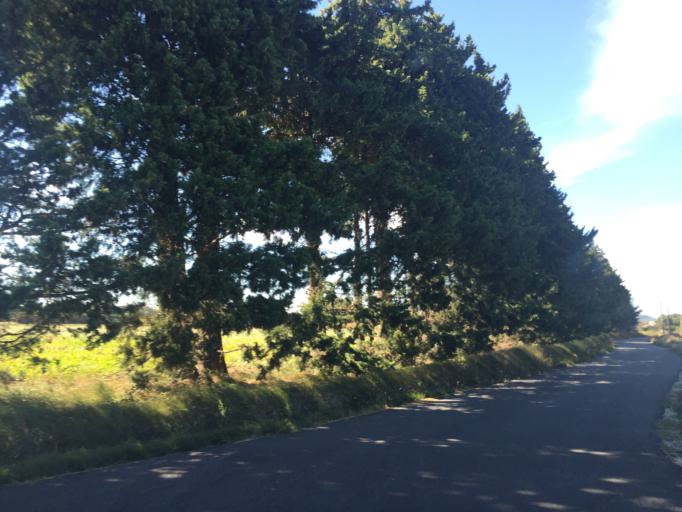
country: FR
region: Provence-Alpes-Cote d'Azur
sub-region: Departement du Vaucluse
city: Orange
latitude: 44.1533
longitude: 4.7873
